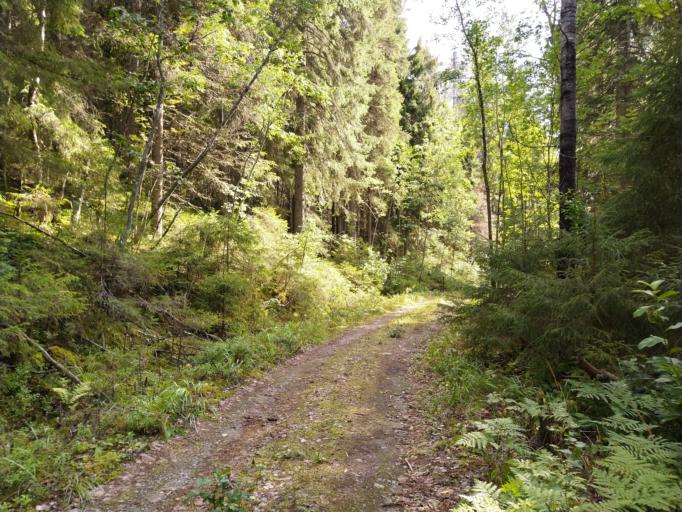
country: FI
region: Paijanne Tavastia
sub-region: Lahti
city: Auttoinen
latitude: 61.2296
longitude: 25.1676
